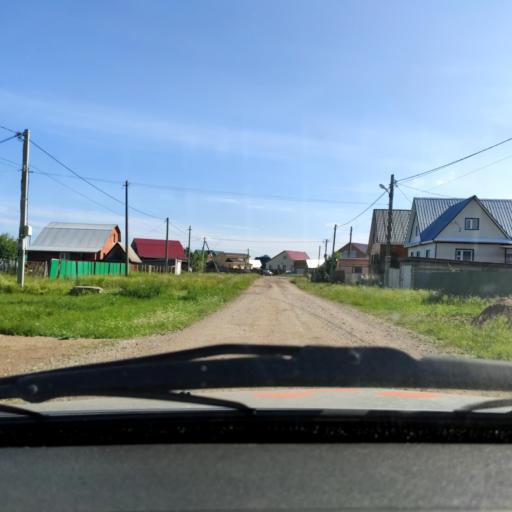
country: RU
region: Bashkortostan
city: Iglino
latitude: 54.7994
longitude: 56.2996
